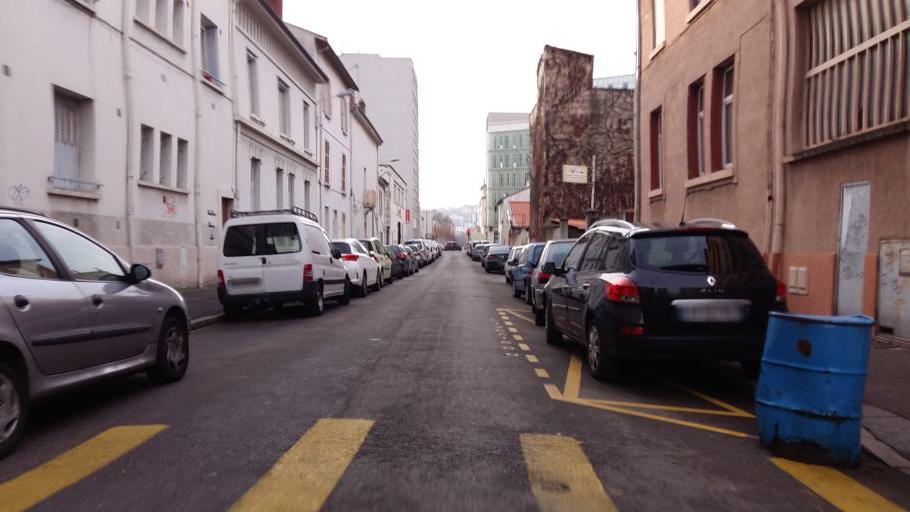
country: FR
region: Rhone-Alpes
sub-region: Departement du Rhone
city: Lyon
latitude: 45.7351
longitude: 4.8374
